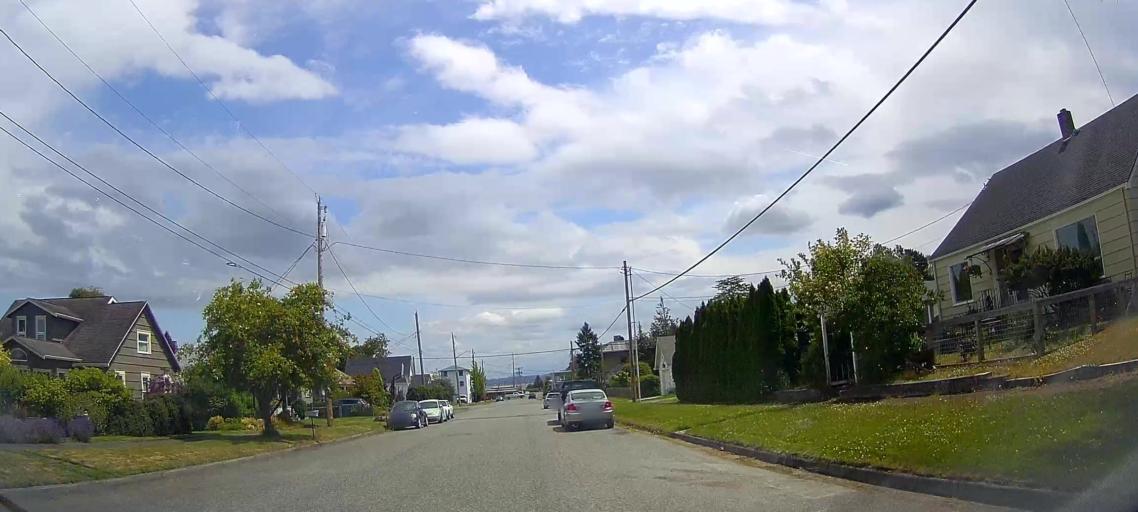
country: US
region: Washington
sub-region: Skagit County
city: Anacortes
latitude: 48.5061
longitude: -122.6154
